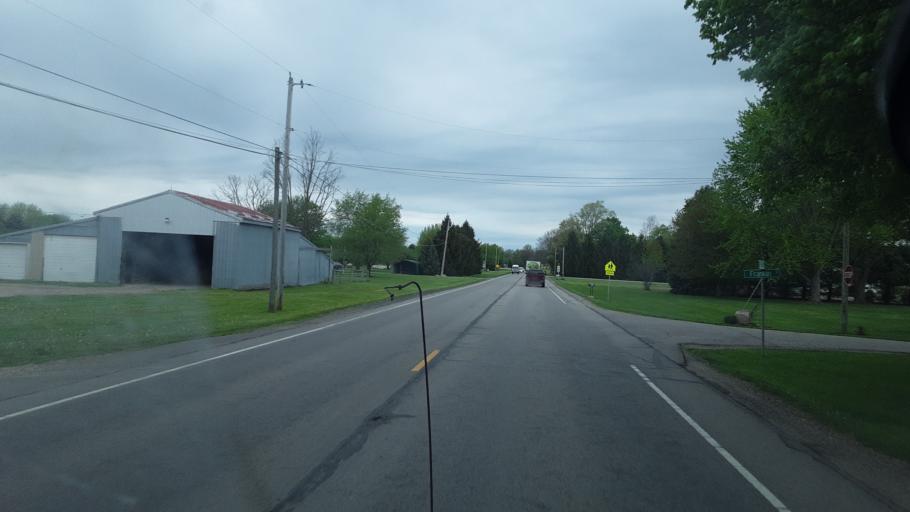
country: US
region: Indiana
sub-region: Elkhart County
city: New Paris
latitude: 41.5127
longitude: -85.7646
